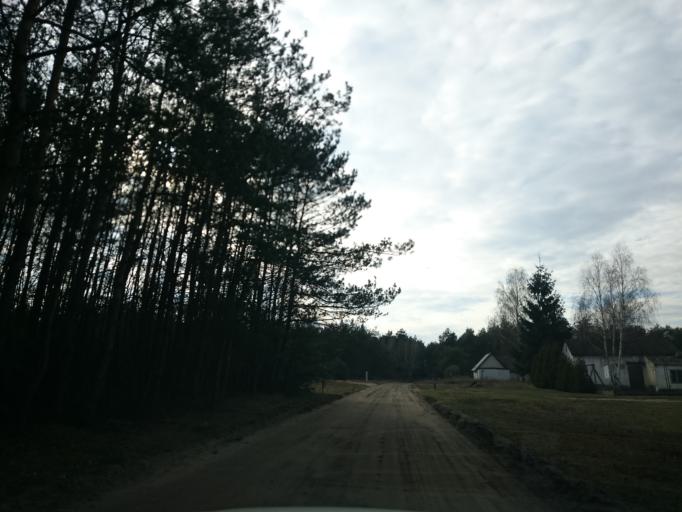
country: PL
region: Kujawsko-Pomorskie
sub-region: Powiat golubsko-dobrzynski
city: Ciechocin
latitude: 53.0494
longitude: 18.8694
